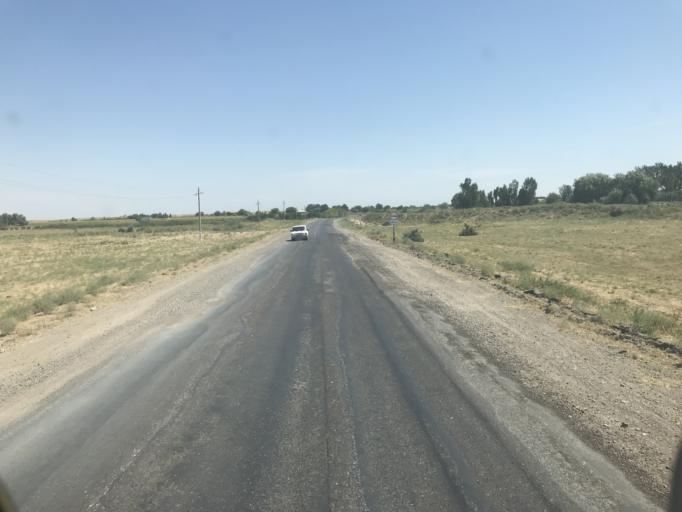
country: UZ
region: Toshkent
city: Yangiyul
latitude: 41.3800
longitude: 68.7870
